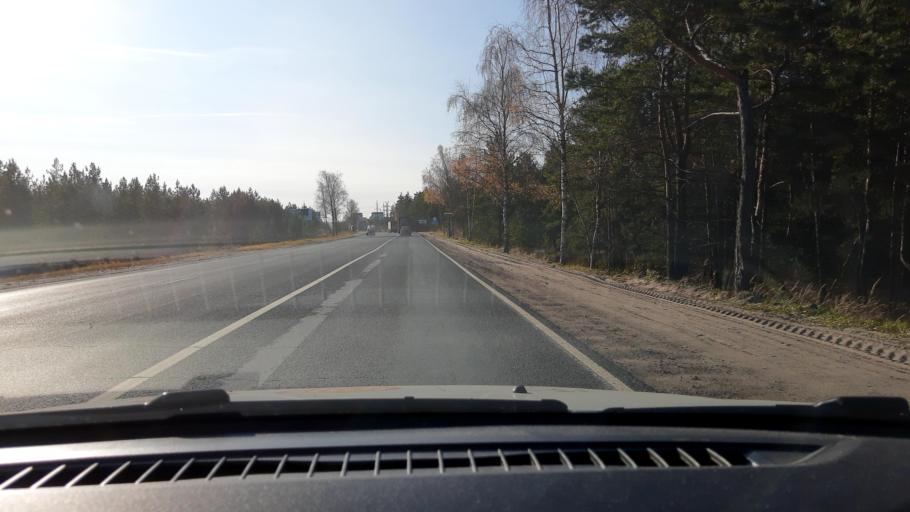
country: RU
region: Nizjnij Novgorod
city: Dzerzhinsk
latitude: 56.2662
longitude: 43.4704
